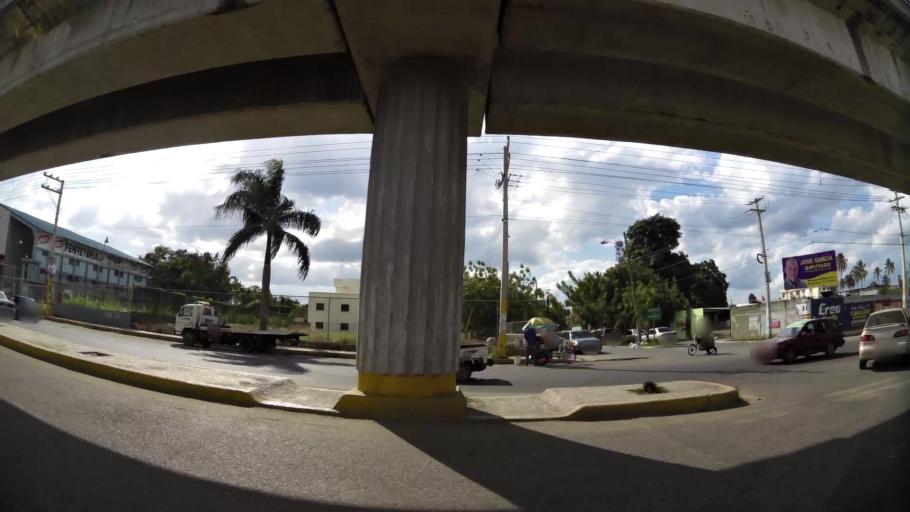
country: DO
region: Nacional
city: Ensanche Luperon
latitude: 18.5489
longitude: -69.9013
